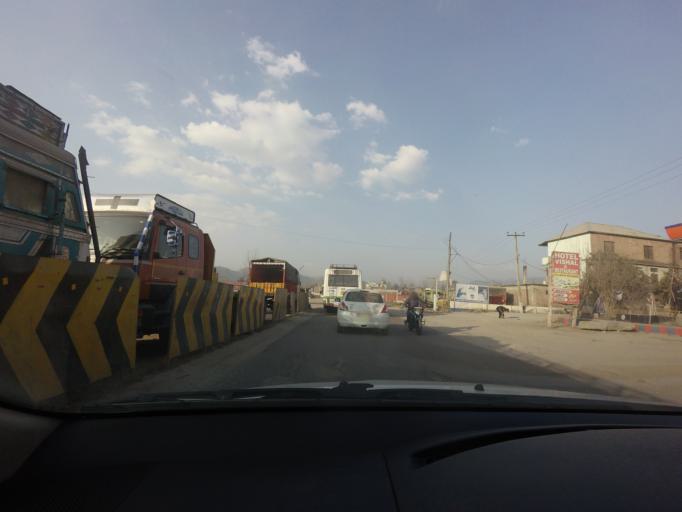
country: IN
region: Himachal Pradesh
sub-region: Mandi
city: Sundarnagar
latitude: 31.5913
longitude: 76.9236
